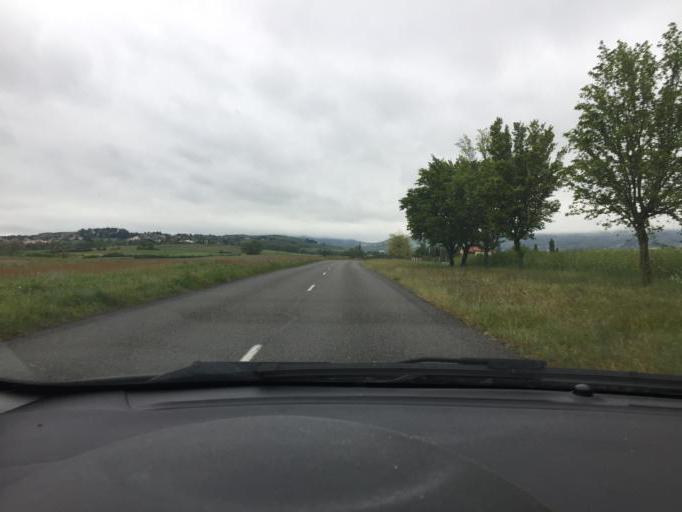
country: FR
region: Rhone-Alpes
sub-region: Departement du Rhone
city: Saint-Maurice-sur-Dargoire
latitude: 45.5894
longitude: 4.6596
